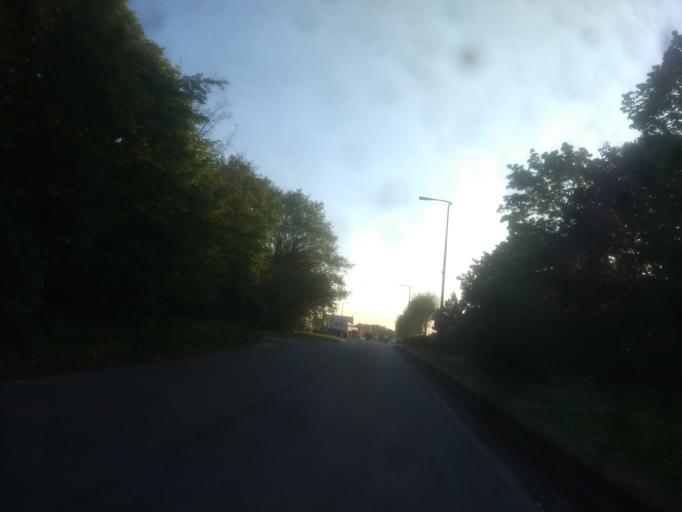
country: FR
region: Nord-Pas-de-Calais
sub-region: Departement du Pas-de-Calais
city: Saint-Laurent-Blangy
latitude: 50.2866
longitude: 2.8114
